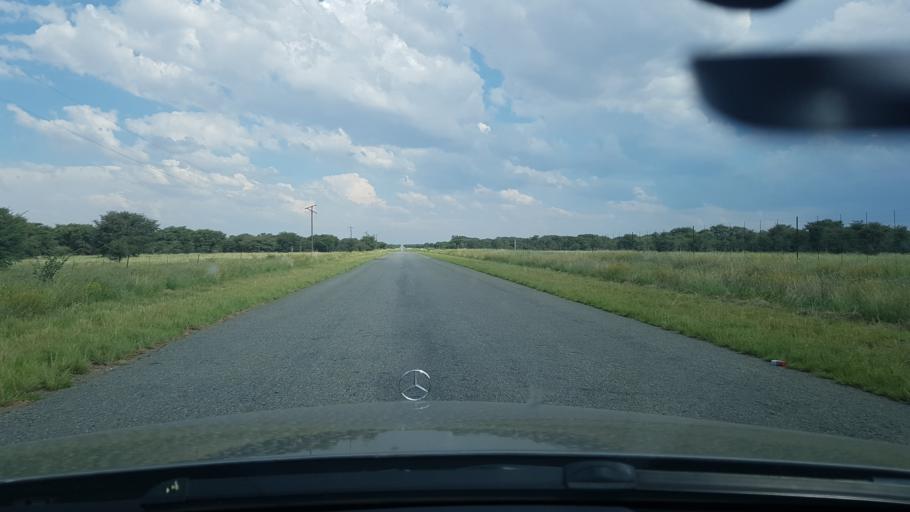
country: ZA
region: North-West
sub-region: Dr Ruth Segomotsi Mompati District Municipality
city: Bloemhof
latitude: -27.7709
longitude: 25.6036
